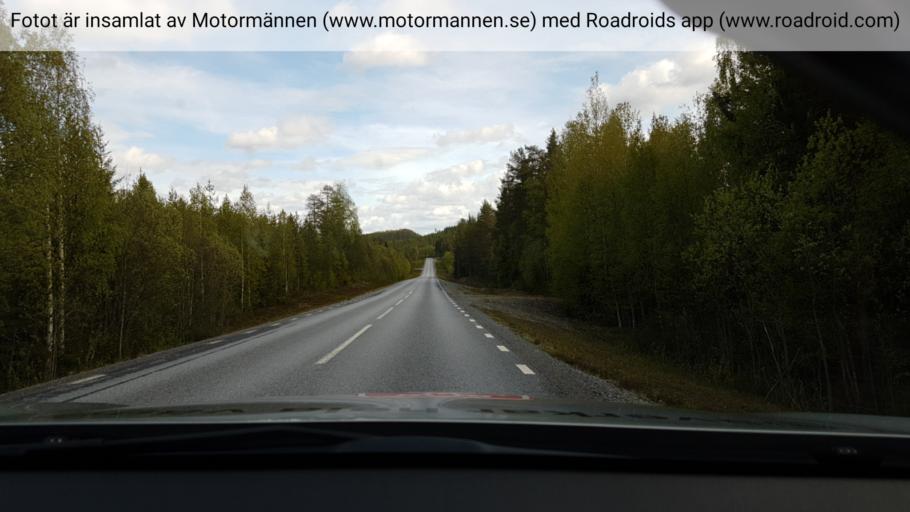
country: SE
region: Vaesterbotten
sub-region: Lycksele Kommun
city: Lycksele
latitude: 64.0456
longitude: 18.5726
